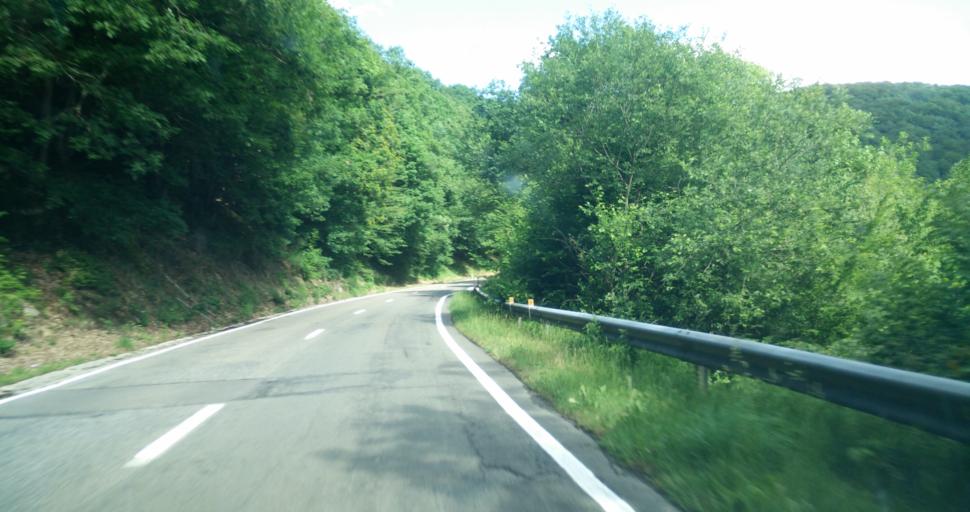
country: BE
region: Wallonia
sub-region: Province du Luxembourg
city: La Roche-en-Ardenne
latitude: 50.1831
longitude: 5.6042
